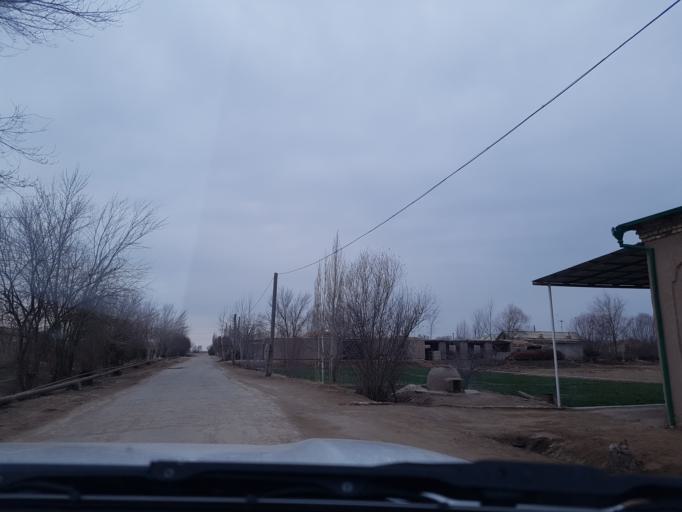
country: TM
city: Akdepe
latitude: 41.9839
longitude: 59.4699
